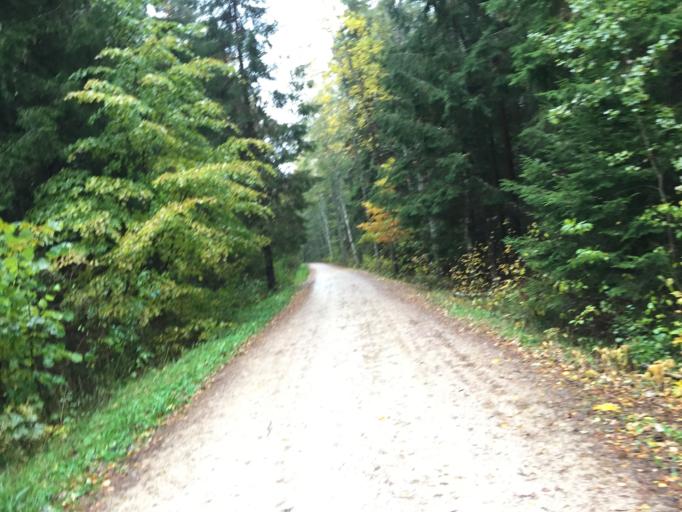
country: LV
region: Engure
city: Smarde
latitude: 56.9158
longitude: 23.4636
